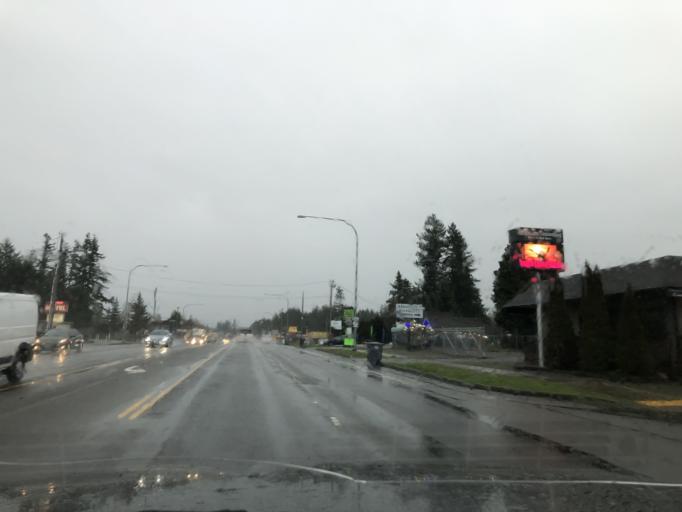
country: US
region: Washington
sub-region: Pierce County
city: Spanaway
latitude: 47.1025
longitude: -122.4349
